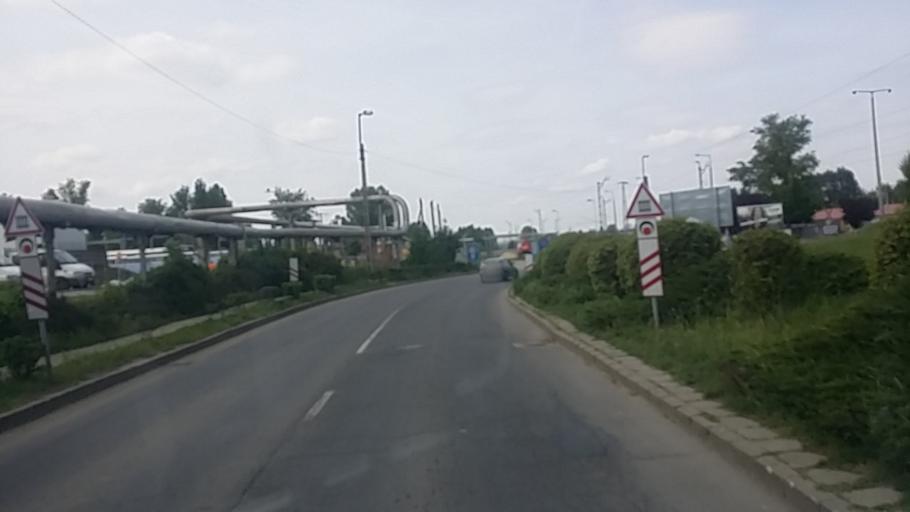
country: HU
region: Komarom-Esztergom
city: Dorog
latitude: 47.7278
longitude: 18.7260
